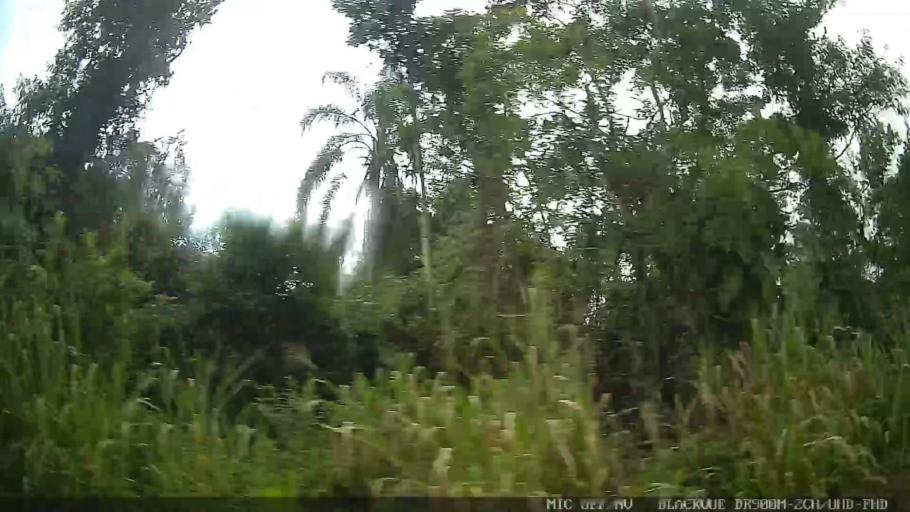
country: BR
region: Sao Paulo
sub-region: Itanhaem
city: Itanhaem
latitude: -24.1144
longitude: -46.7951
